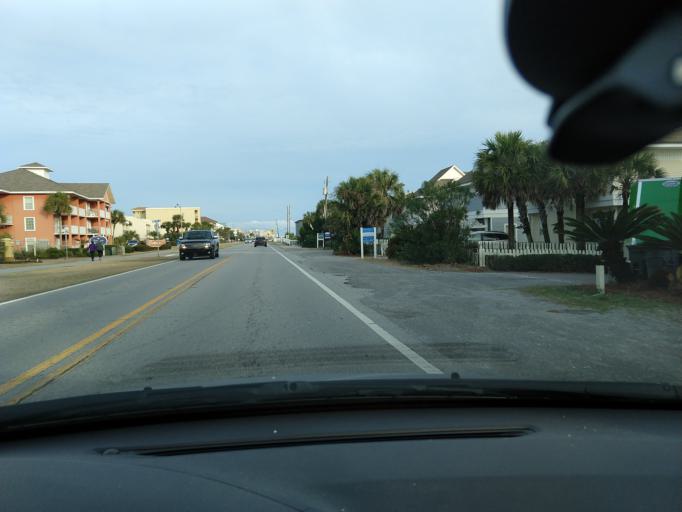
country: US
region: Florida
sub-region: Walton County
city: Miramar Beach
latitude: 30.3793
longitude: -86.3958
